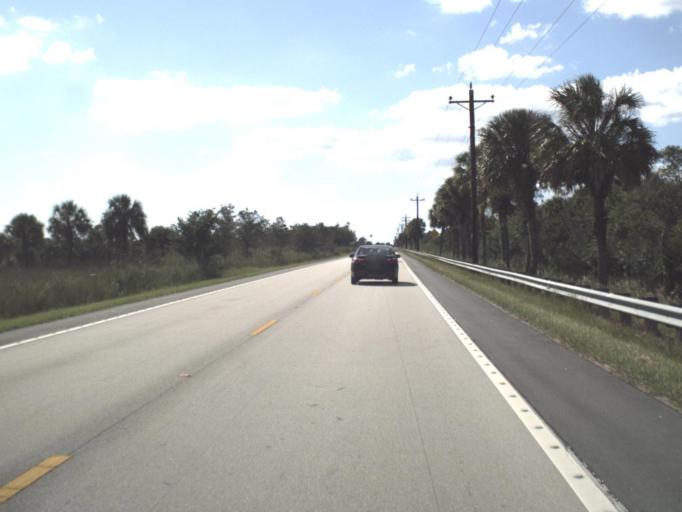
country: US
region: Florida
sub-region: Collier County
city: Marco
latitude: 25.9015
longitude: -81.3179
